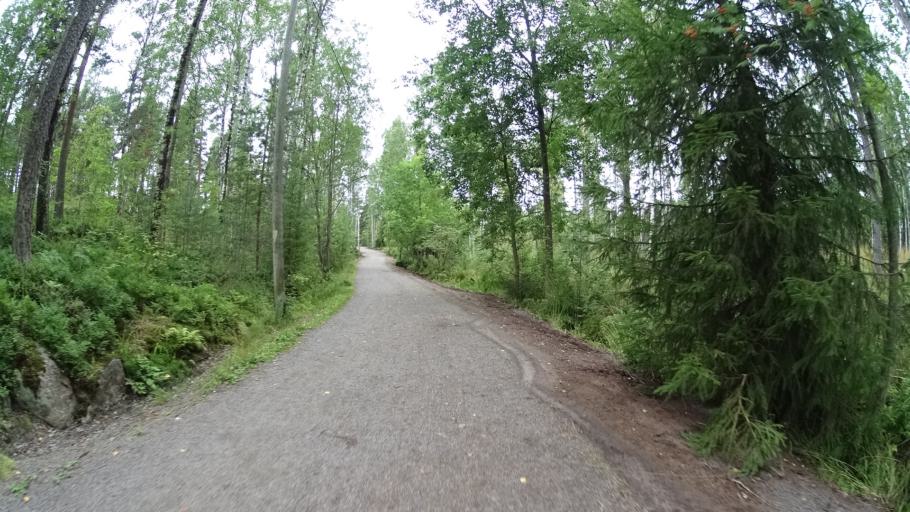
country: FI
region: Uusimaa
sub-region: Helsinki
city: Kilo
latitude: 60.2276
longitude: 24.7550
